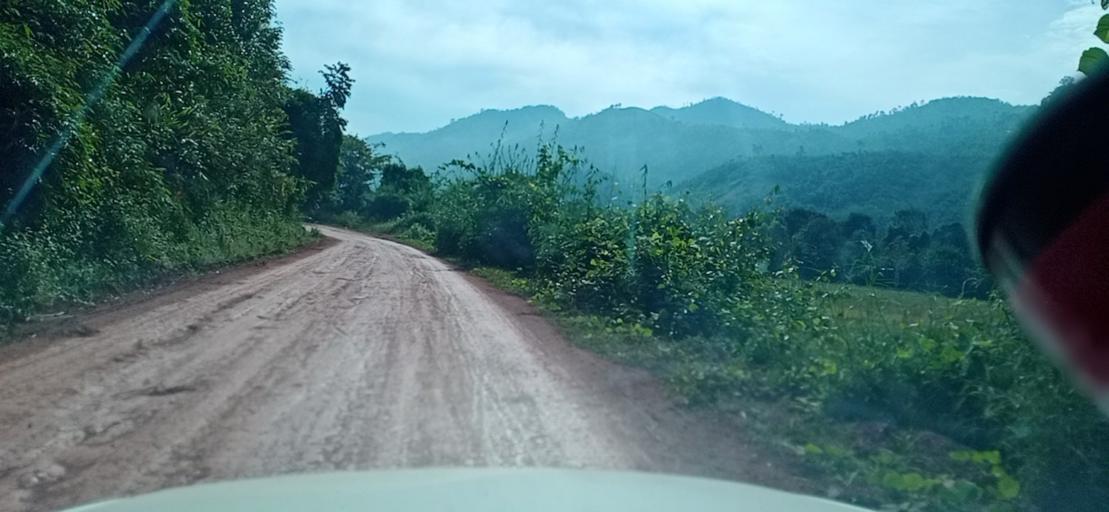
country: TH
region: Changwat Bueng Kan
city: Pak Khat
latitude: 18.6701
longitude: 103.1960
